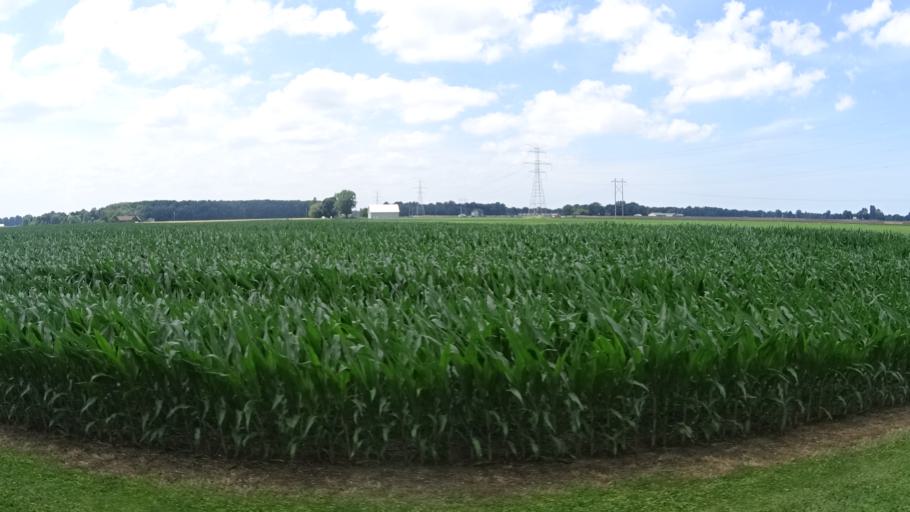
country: US
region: Ohio
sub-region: Erie County
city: Huron
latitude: 41.3345
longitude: -82.5369
